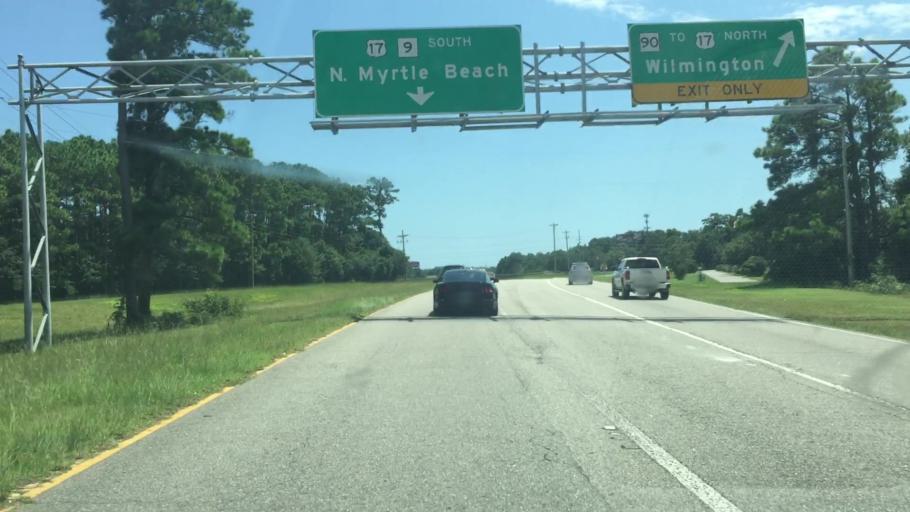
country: US
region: South Carolina
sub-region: Horry County
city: Little River
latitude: 33.8624
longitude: -78.6582
